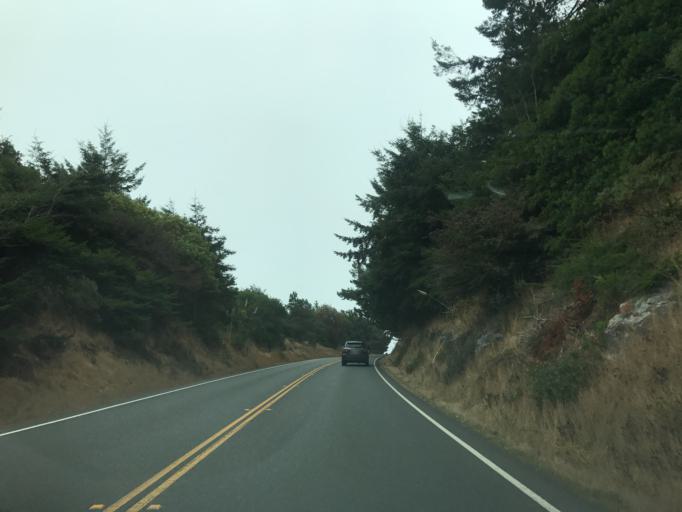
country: US
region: California
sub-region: Sonoma County
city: Sea Ranch
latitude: 38.7577
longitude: -123.5163
